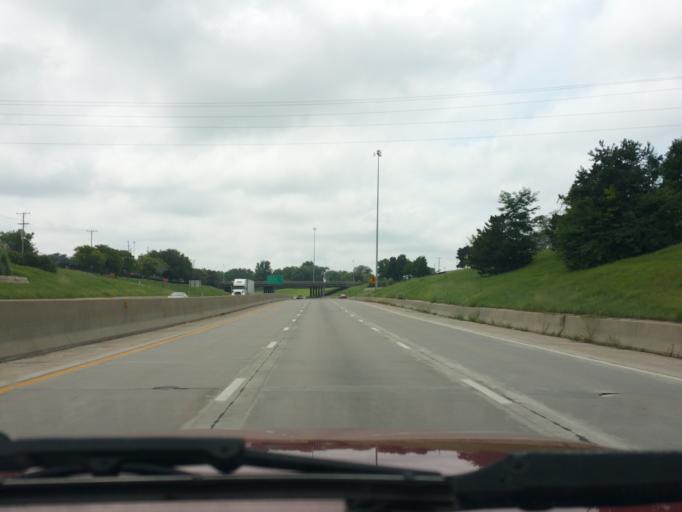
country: US
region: Kansas
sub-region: Shawnee County
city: Topeka
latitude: 39.0479
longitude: -95.6709
